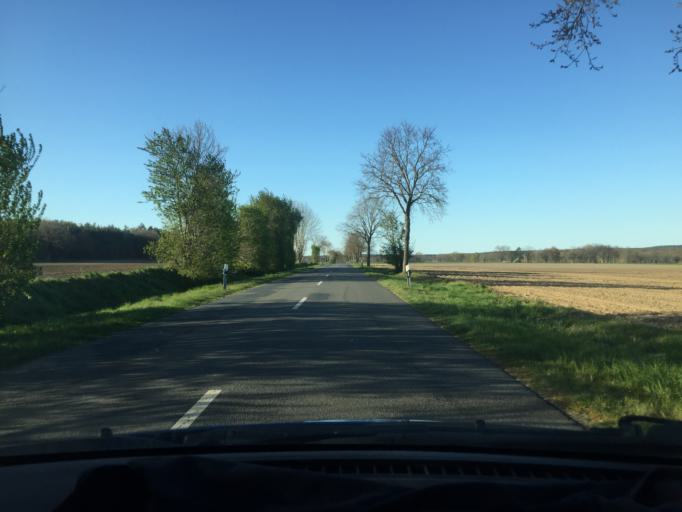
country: DE
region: Lower Saxony
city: Himbergen
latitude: 53.0752
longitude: 10.7296
